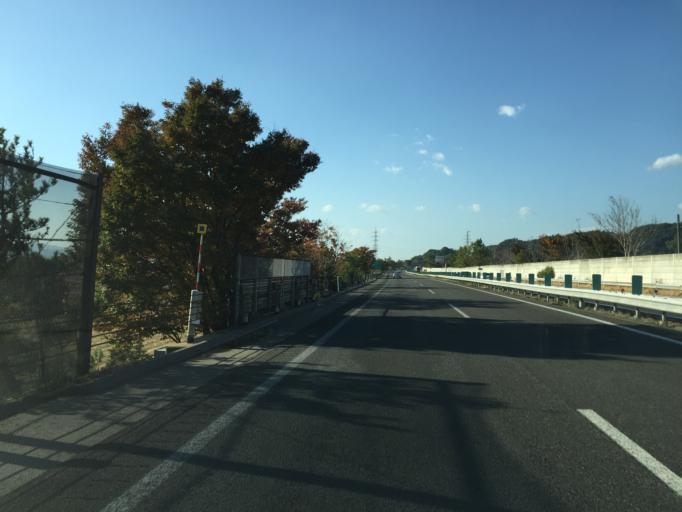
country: JP
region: Fukushima
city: Hobaramachi
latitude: 37.8735
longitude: 140.5239
